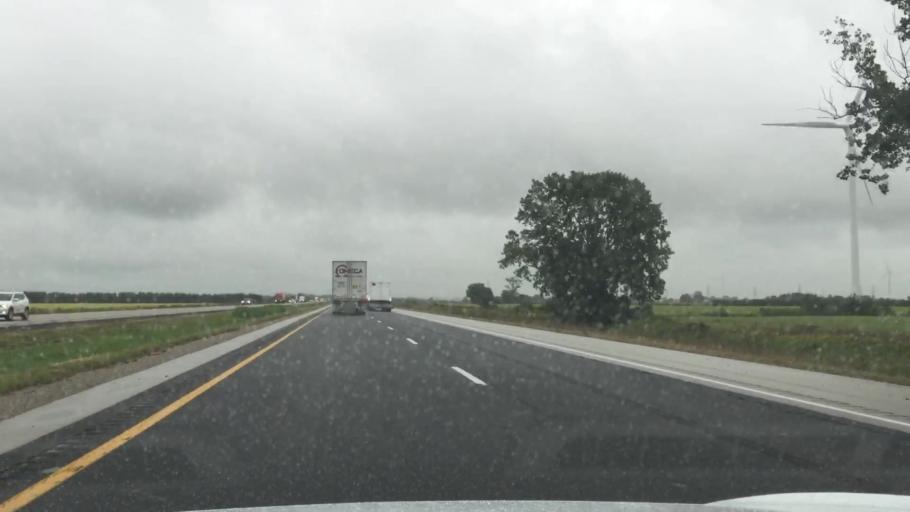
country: CA
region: Ontario
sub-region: Lambton County
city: Walpole Island
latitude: 42.3269
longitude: -82.2371
